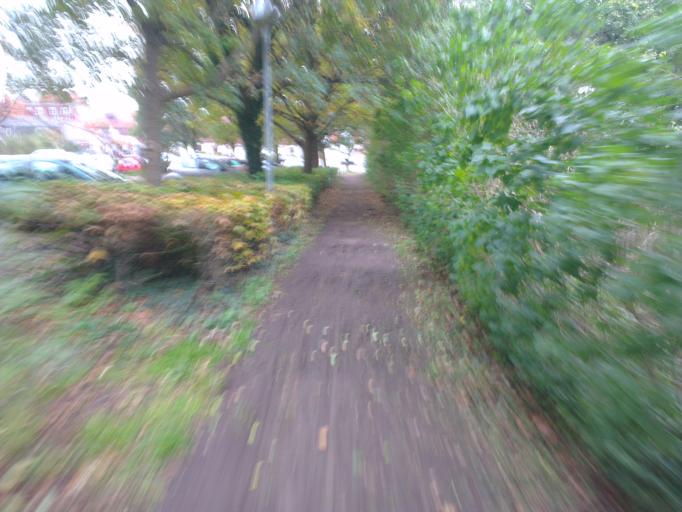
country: DK
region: Capital Region
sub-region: Frederikssund Kommune
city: Frederikssund
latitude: 55.8374
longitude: 12.0621
